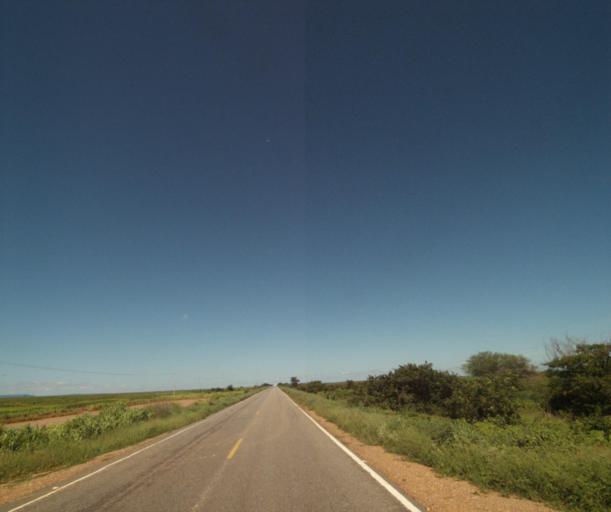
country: BR
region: Bahia
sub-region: Palmas De Monte Alto
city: Palmas de Monte Alto
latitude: -14.2695
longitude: -43.4057
